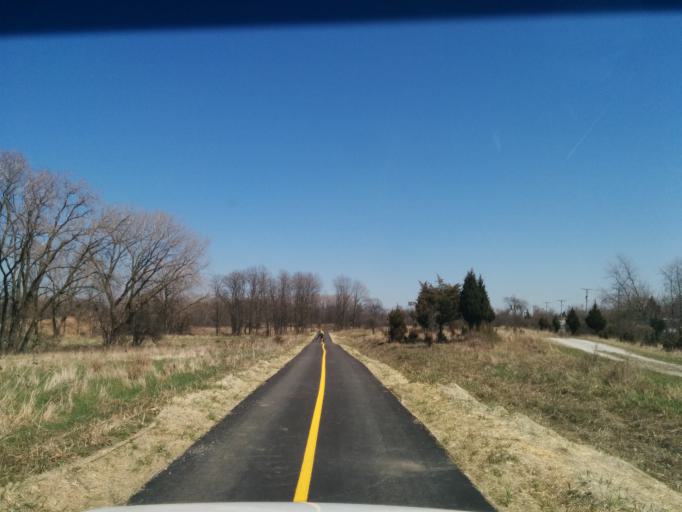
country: US
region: Illinois
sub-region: Cook County
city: Oak Forest
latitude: 41.5963
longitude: -87.7267
